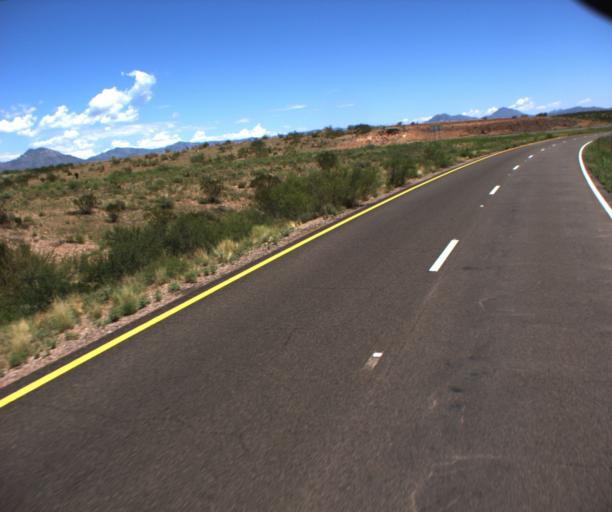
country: US
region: Arizona
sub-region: Greenlee County
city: Clifton
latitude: 32.9681
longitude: -109.2361
